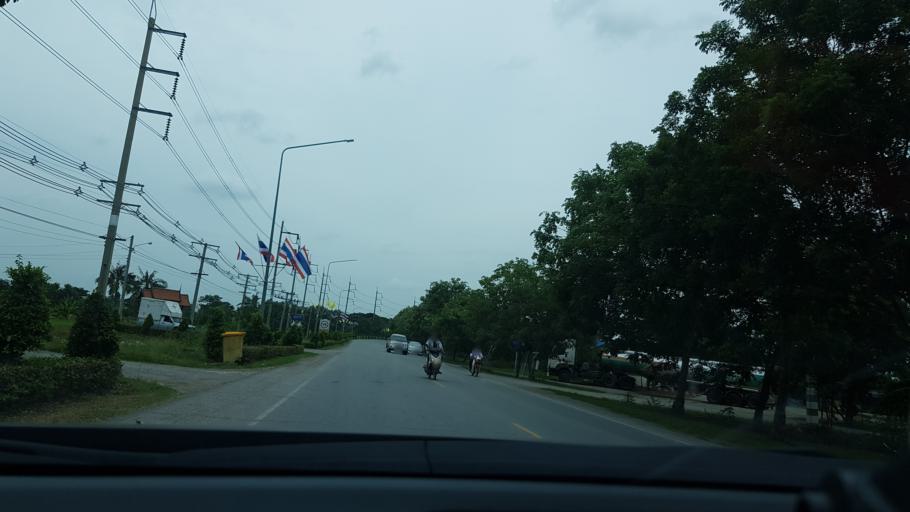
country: TH
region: Phra Nakhon Si Ayutthaya
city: Bang Pa-in
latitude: 14.1677
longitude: 100.5173
